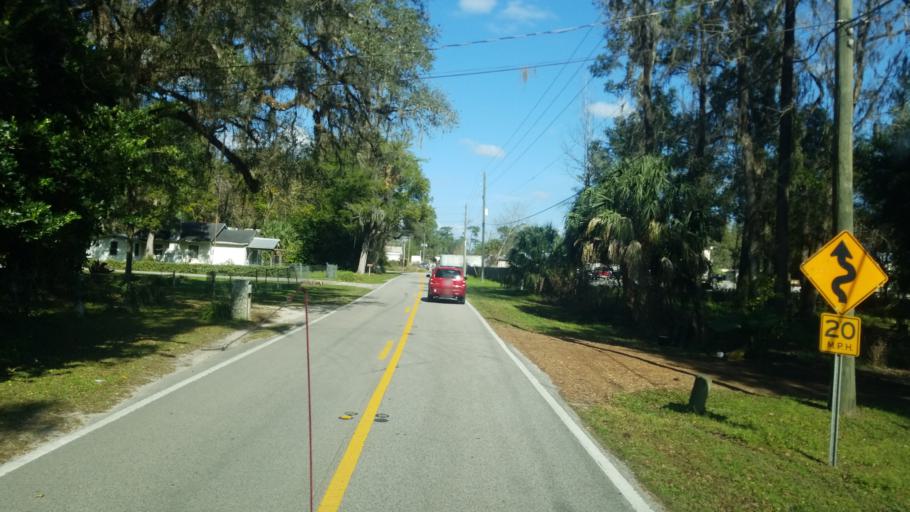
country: US
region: Florida
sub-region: Hernando County
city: Brooksville
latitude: 28.5898
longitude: -82.3747
